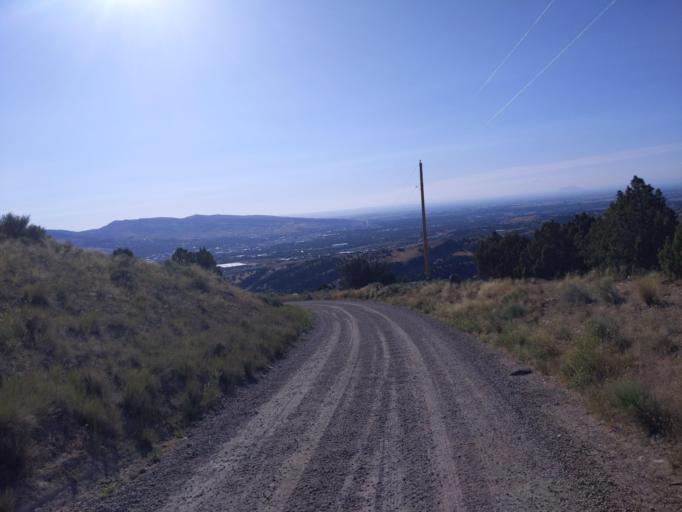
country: US
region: Idaho
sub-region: Bannock County
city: Pocatello
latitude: 42.8535
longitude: -112.3830
